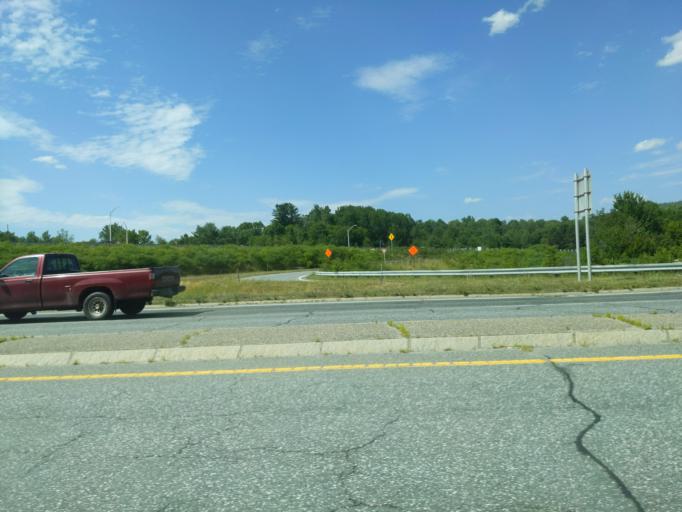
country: US
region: New Hampshire
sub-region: Grafton County
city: Lebanon
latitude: 43.6377
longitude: -72.2793
